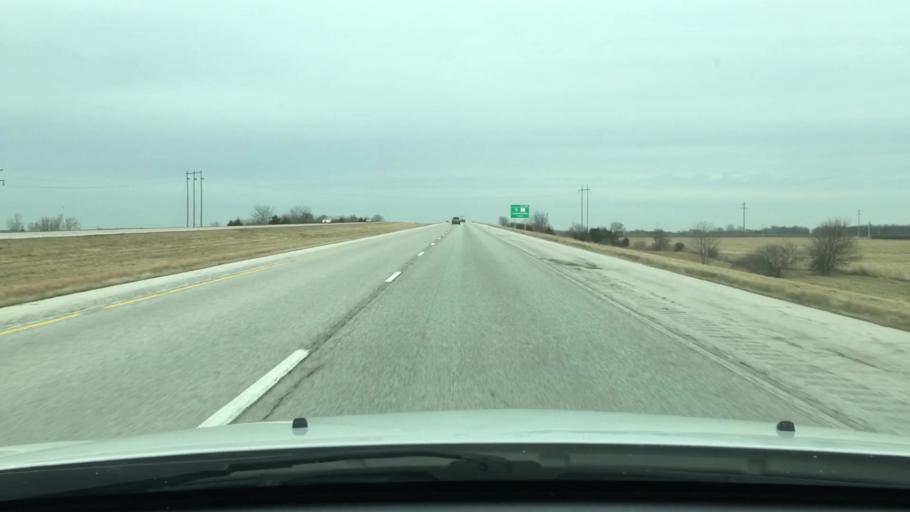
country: US
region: Illinois
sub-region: Morgan County
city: South Jacksonville
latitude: 39.7061
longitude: -90.1846
